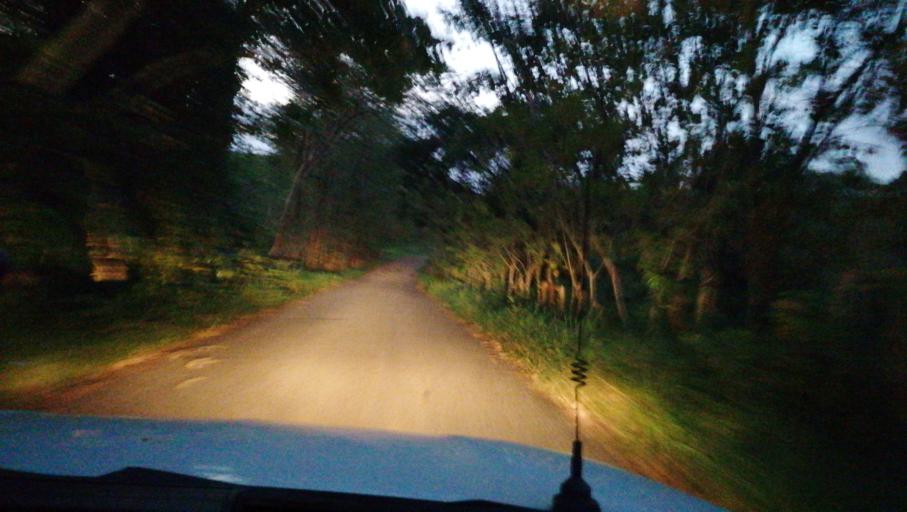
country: MX
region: Chiapas
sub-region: Ostuacan
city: Nuevo Juan del Grijalva
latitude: 17.4777
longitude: -93.3460
